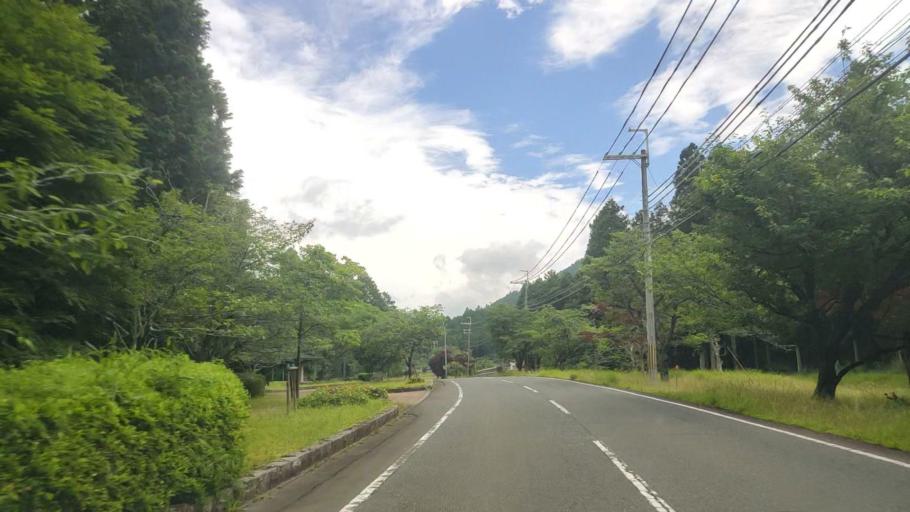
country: JP
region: Kyoto
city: Fukuchiyama
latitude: 35.1934
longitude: 134.9339
